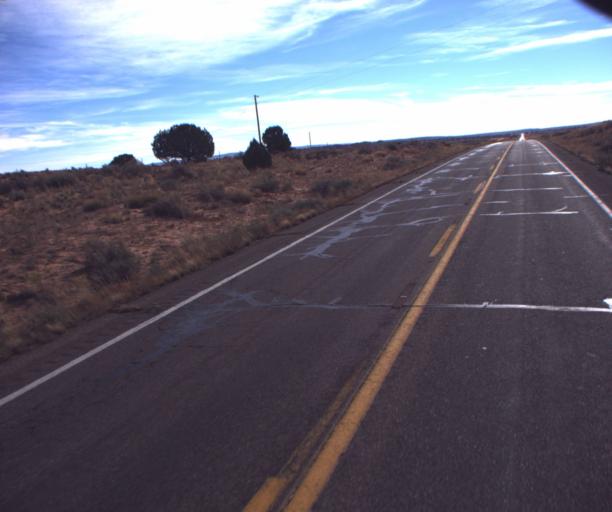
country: US
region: Arizona
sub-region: Coconino County
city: Kaibito
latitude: 36.6161
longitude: -111.1923
